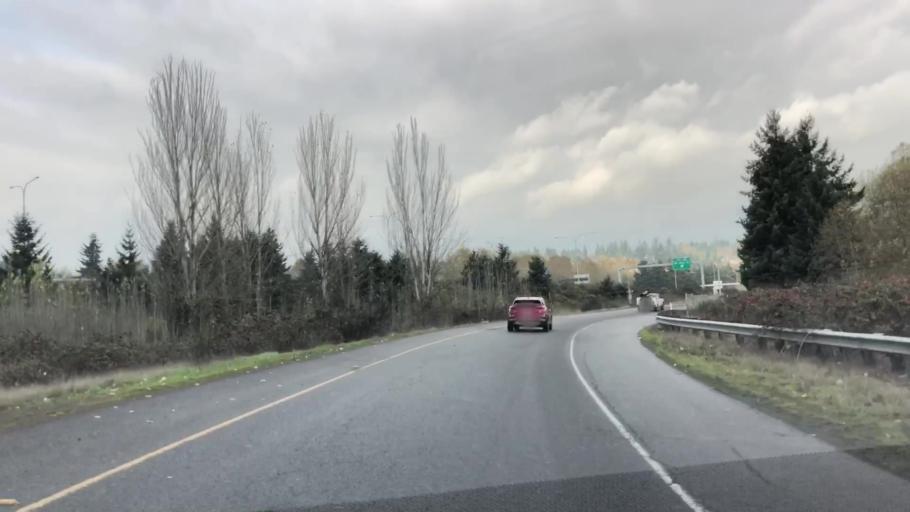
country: US
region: Washington
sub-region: King County
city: Woodinville
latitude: 47.7595
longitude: -122.1824
